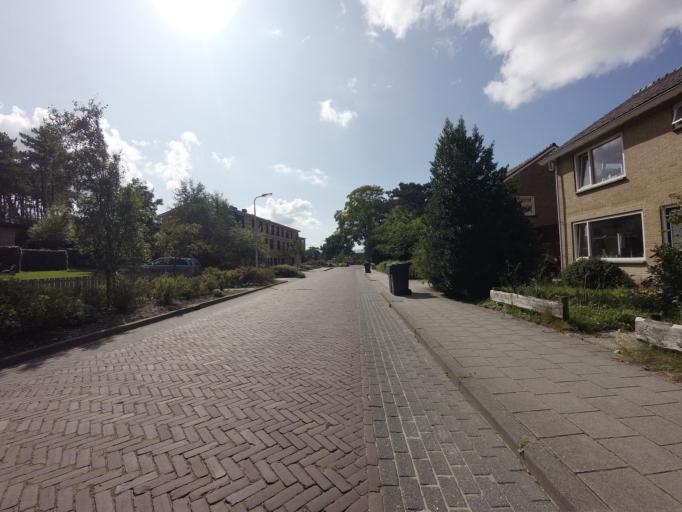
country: NL
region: Friesland
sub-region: Gemeente Terschelling
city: West-Terschelling
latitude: 53.3654
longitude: 5.2150
